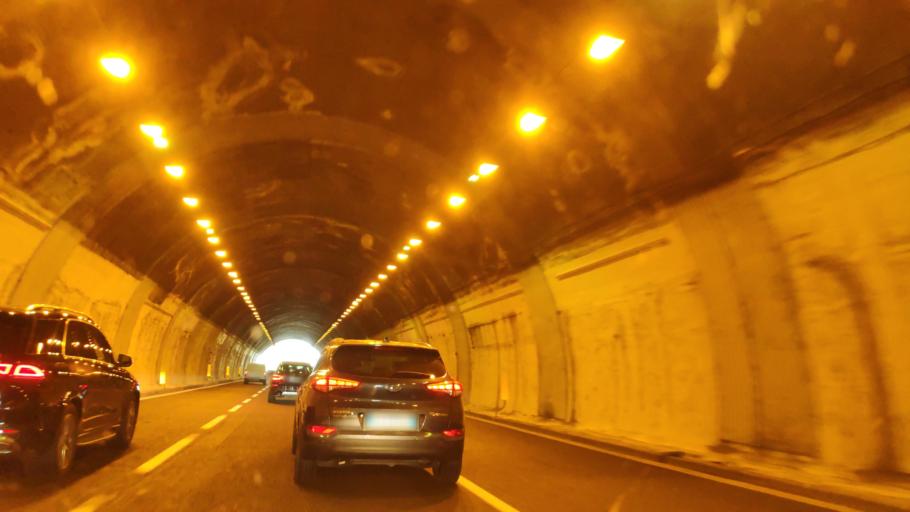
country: IT
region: Campania
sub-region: Provincia di Salerno
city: Mercato San Severino
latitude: 40.7708
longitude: 14.7415
